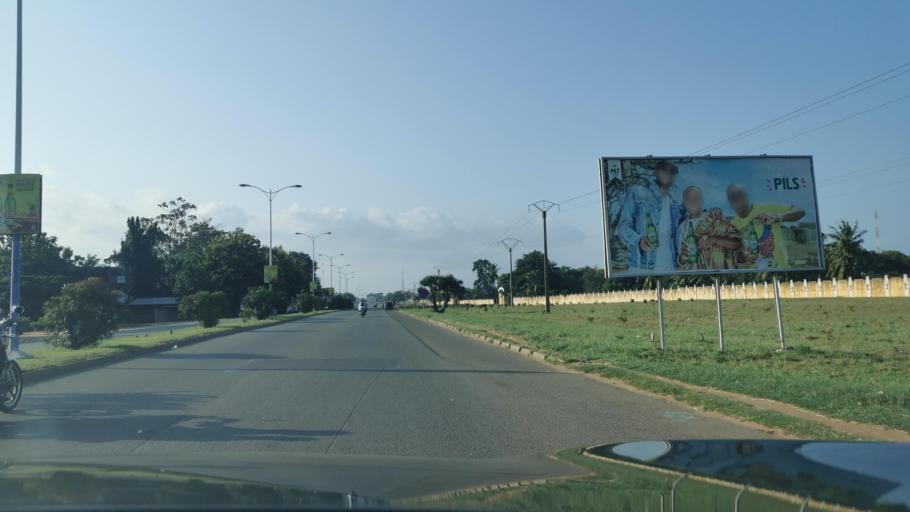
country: TG
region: Maritime
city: Lome
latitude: 6.2059
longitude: 1.2087
